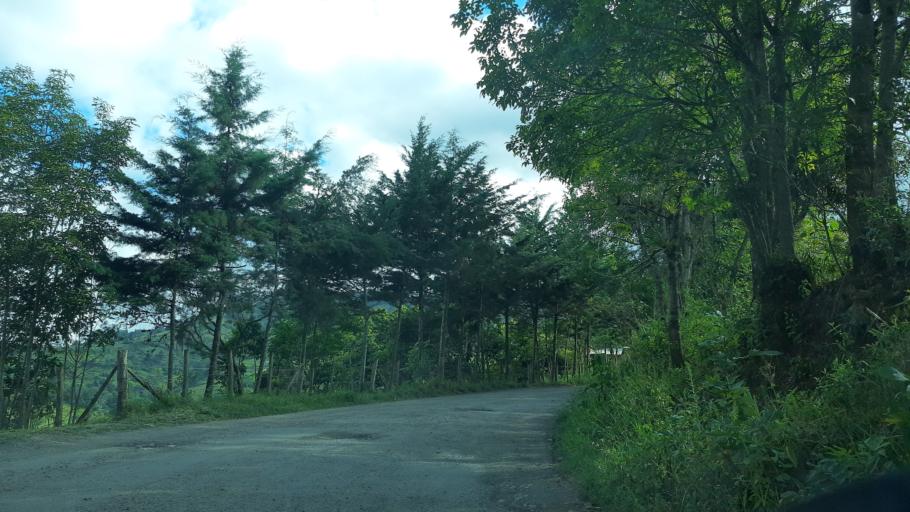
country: CO
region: Cundinamarca
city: Tenza
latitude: 5.0549
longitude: -73.4164
